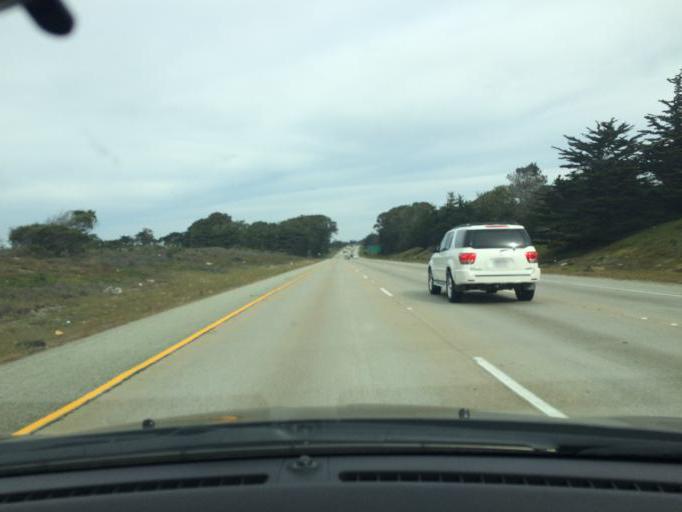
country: US
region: California
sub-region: Monterey County
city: Seaside
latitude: 36.6396
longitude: -121.8262
